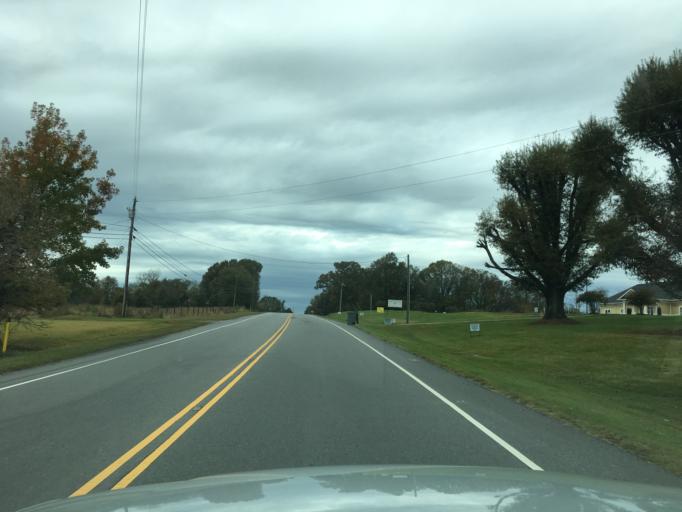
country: US
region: North Carolina
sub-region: Catawba County
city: Maiden
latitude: 35.5959
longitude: -81.2509
